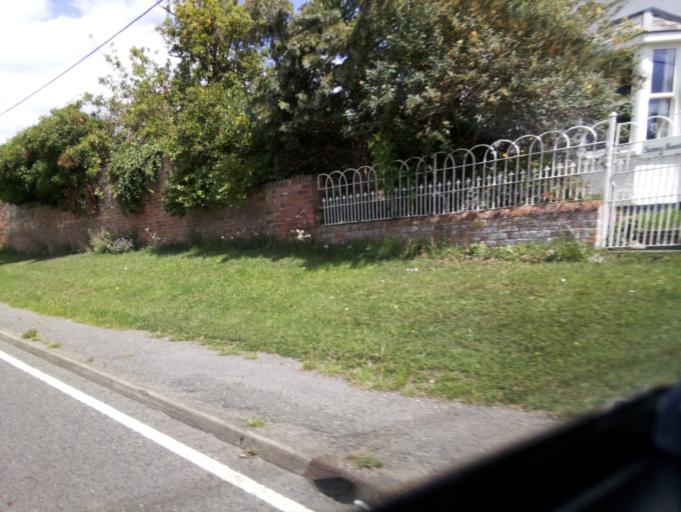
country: GB
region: England
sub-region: Buckinghamshire
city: Aylesbury
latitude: 51.8631
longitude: -0.8312
